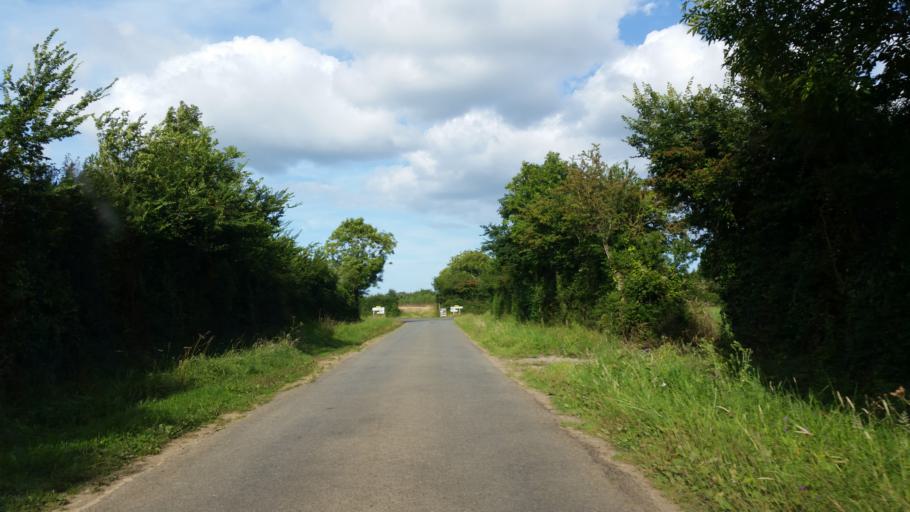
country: FR
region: Lower Normandy
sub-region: Departement de la Manche
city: Sainte-Mere-Eglise
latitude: 49.4627
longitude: -1.3040
